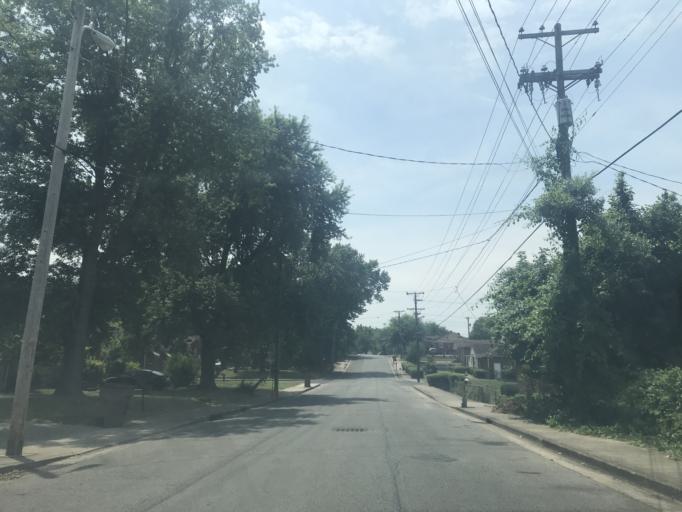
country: US
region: Tennessee
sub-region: Davidson County
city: Nashville
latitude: 36.1820
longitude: -86.8194
